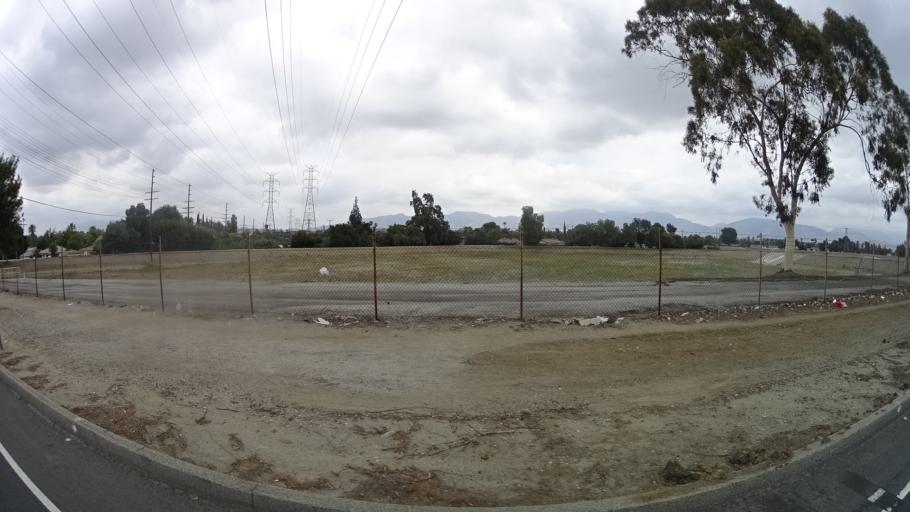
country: US
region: California
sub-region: Los Angeles County
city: San Fernando
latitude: 34.2573
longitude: -118.4517
